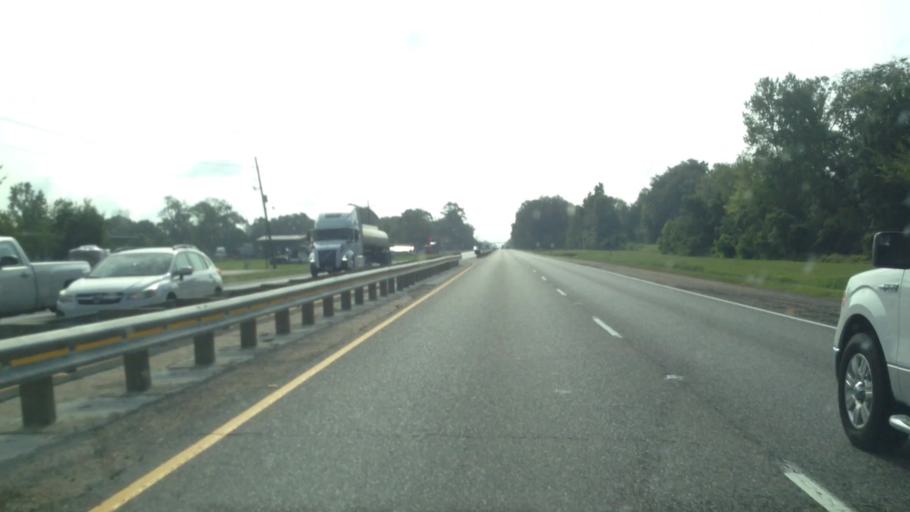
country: US
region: Louisiana
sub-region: Pointe Coupee Parish
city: Livonia
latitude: 30.5550
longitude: -91.5709
